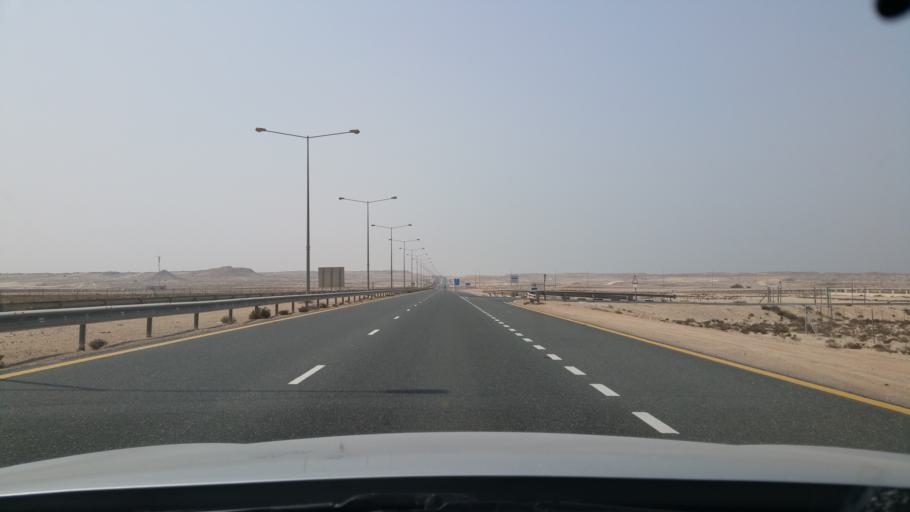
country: QA
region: Baladiyat ar Rayyan
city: Dukhan
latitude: 25.3761
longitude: 50.7811
